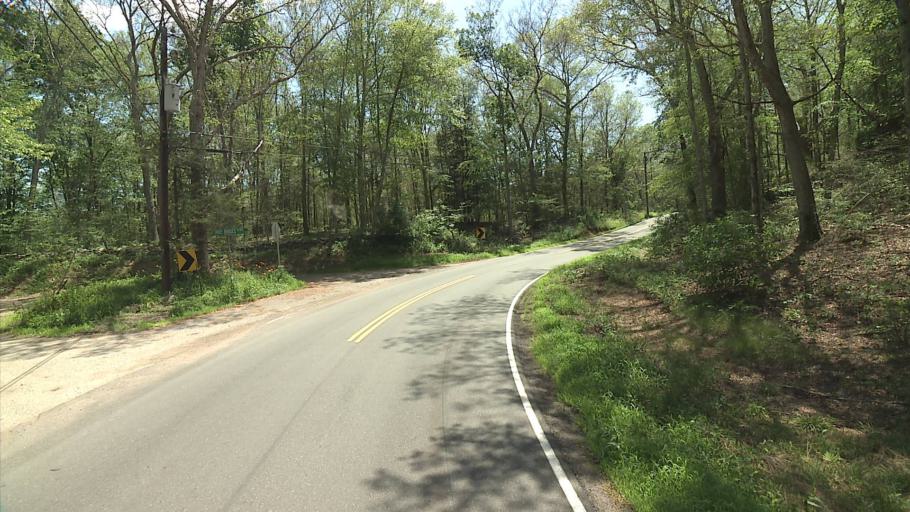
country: US
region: Connecticut
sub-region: Middlesex County
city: Essex Village
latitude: 41.4454
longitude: -72.3365
